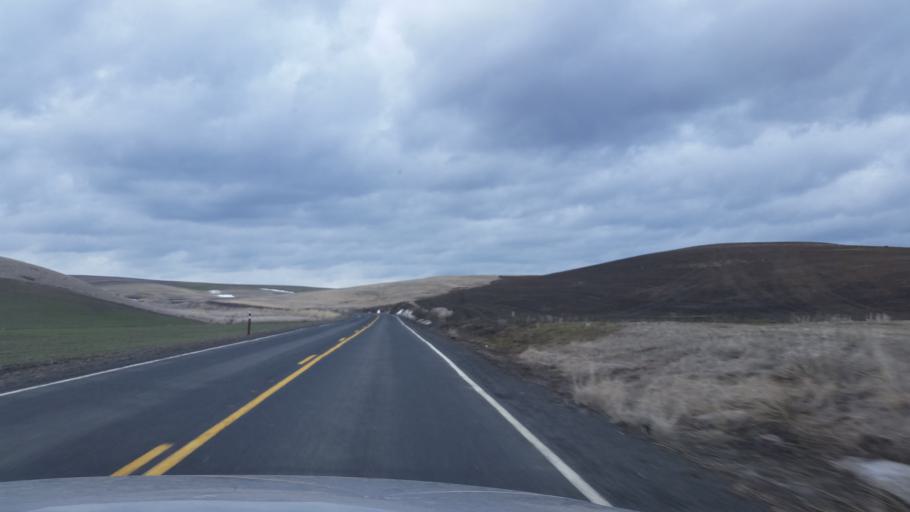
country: US
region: Washington
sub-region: Spokane County
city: Cheney
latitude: 47.1861
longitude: -117.8712
